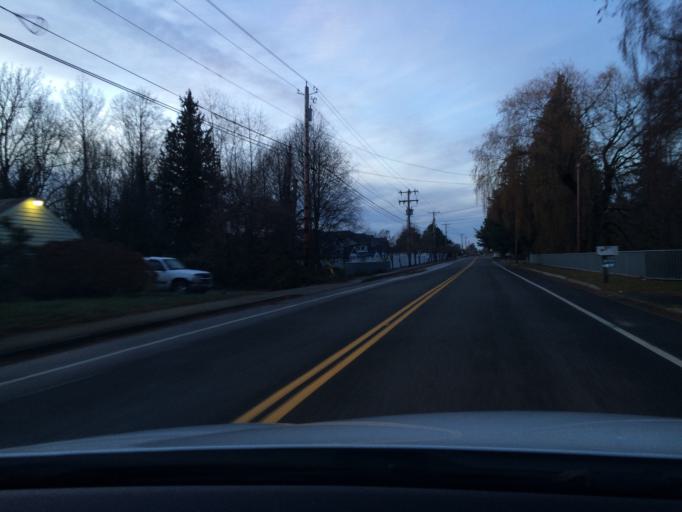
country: US
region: Washington
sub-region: Whatcom County
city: Marietta-Alderwood
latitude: 48.7731
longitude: -122.5283
